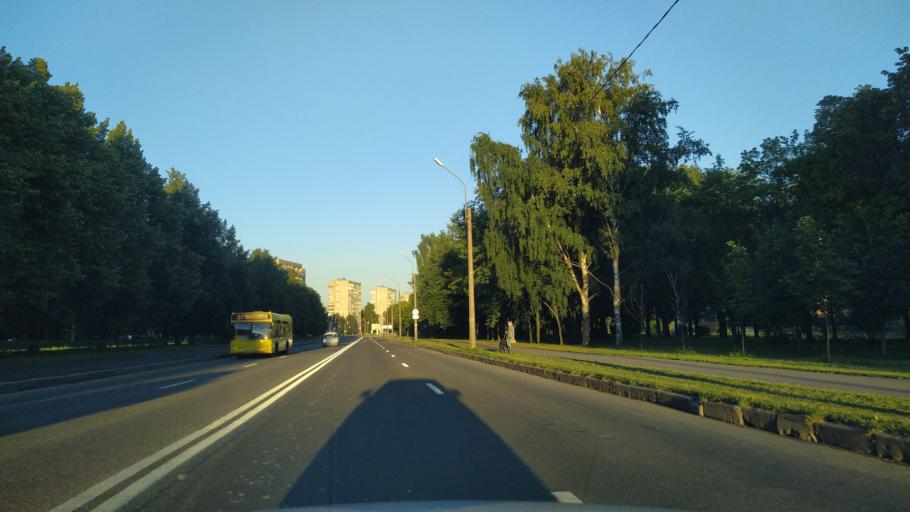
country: RU
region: Leningrad
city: Kalininskiy
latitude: 59.9645
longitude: 30.4033
